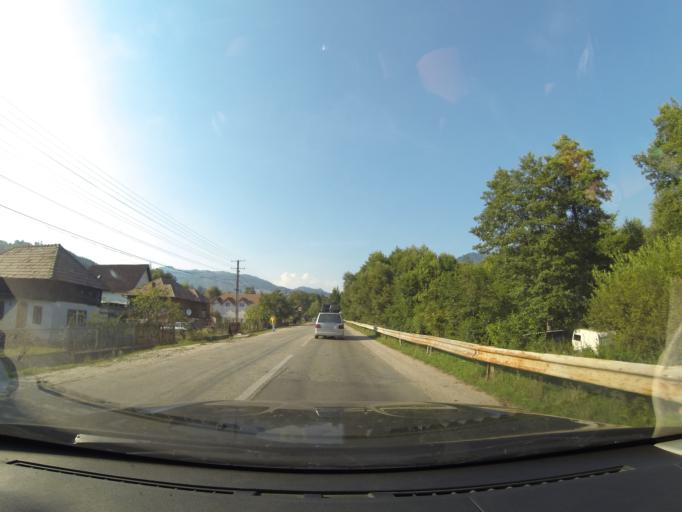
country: RO
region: Arges
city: Poenari
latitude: 45.3213
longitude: 24.6399
